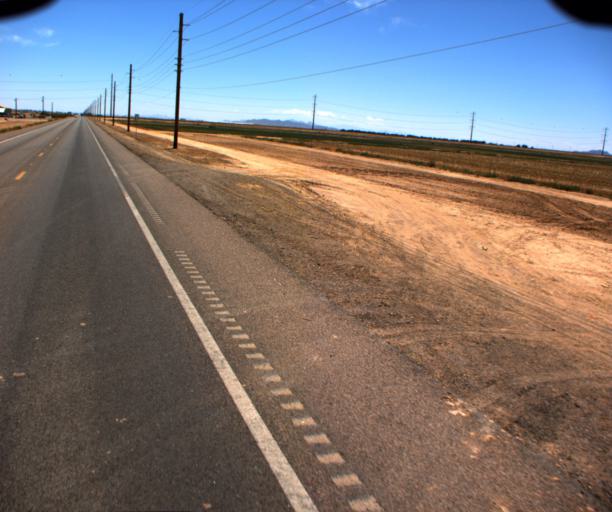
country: US
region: Arizona
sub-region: Pinal County
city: Casa Grande
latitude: 32.8794
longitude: -111.9539
